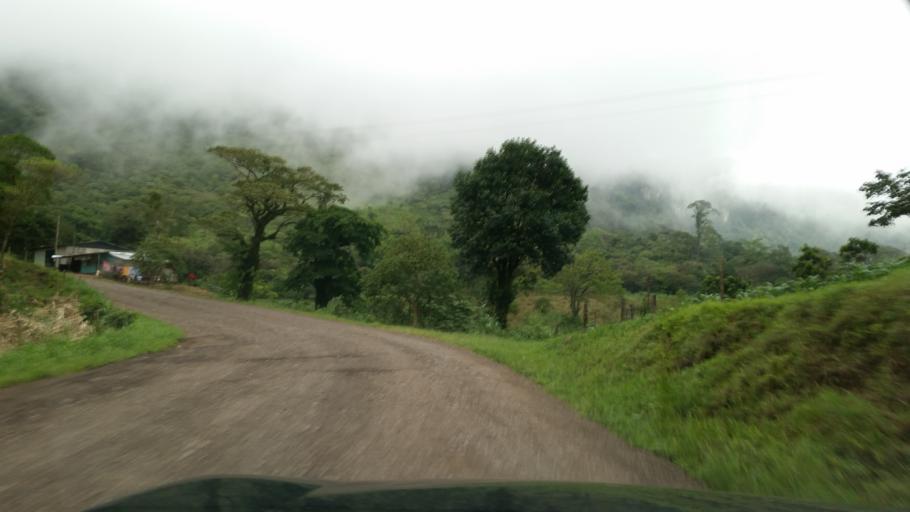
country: NI
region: Jinotega
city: San Jose de Bocay
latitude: 13.2822
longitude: -85.7181
